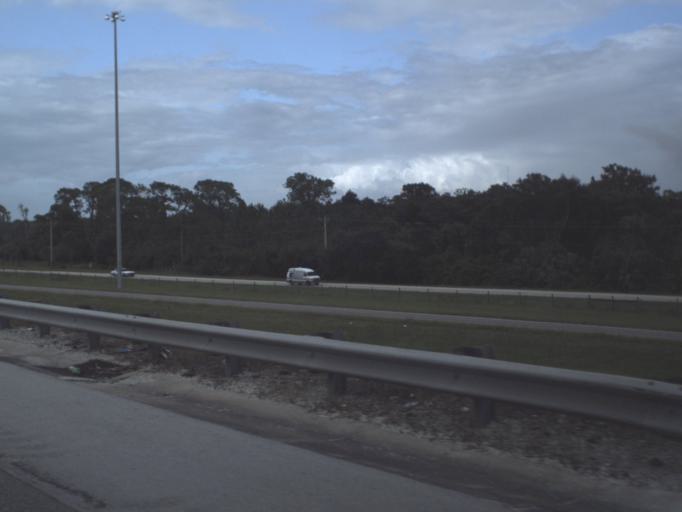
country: US
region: Florida
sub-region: Lee County
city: Tice
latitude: 26.7158
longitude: -81.8121
